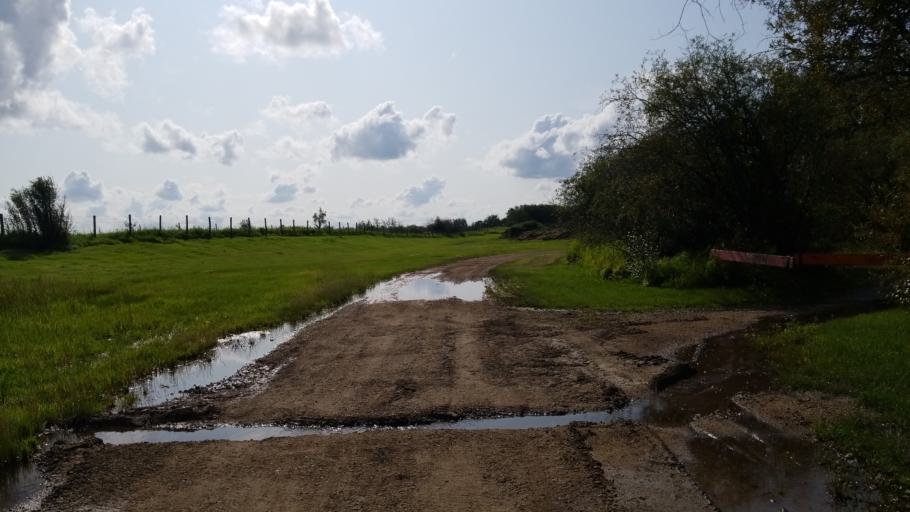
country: CA
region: Saskatchewan
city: Lloydminster
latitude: 53.2565
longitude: -110.0451
